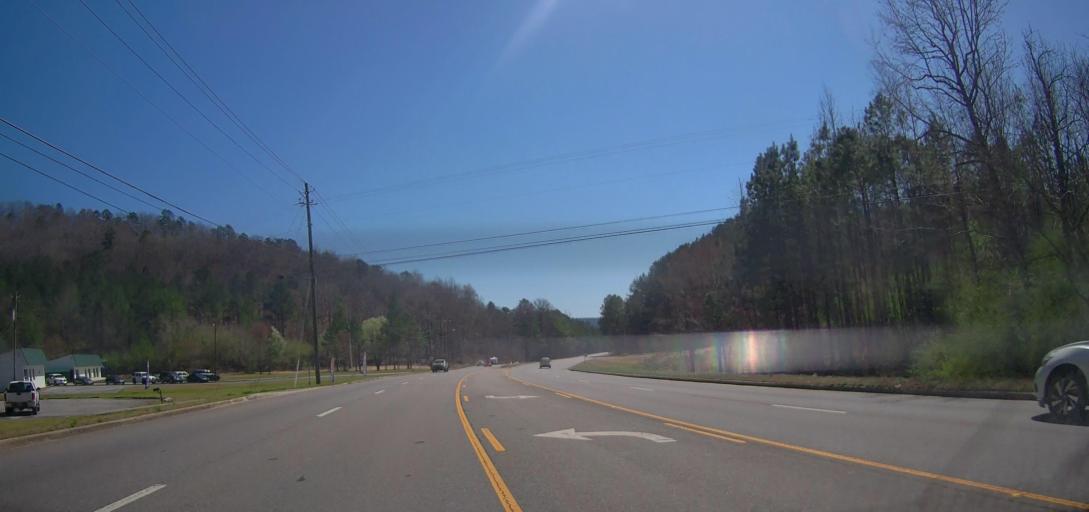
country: US
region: Alabama
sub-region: Etowah County
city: Rainbow City
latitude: 33.9499
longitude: -86.0322
